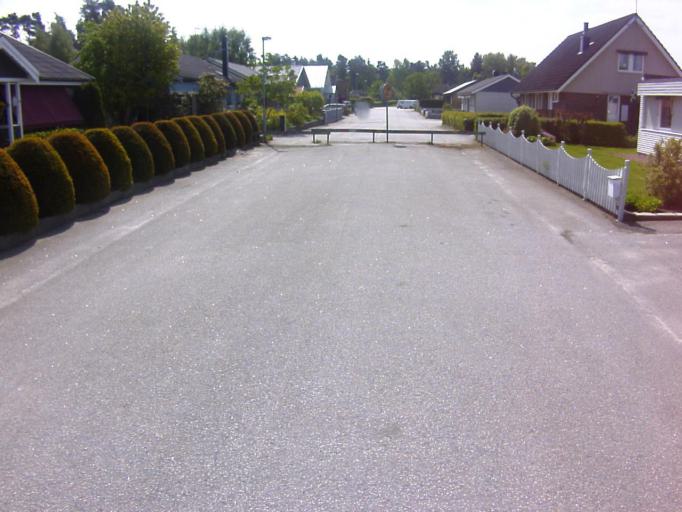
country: SE
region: Blekinge
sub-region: Solvesborgs Kommun
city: Soelvesborg
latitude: 56.0398
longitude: 14.5647
